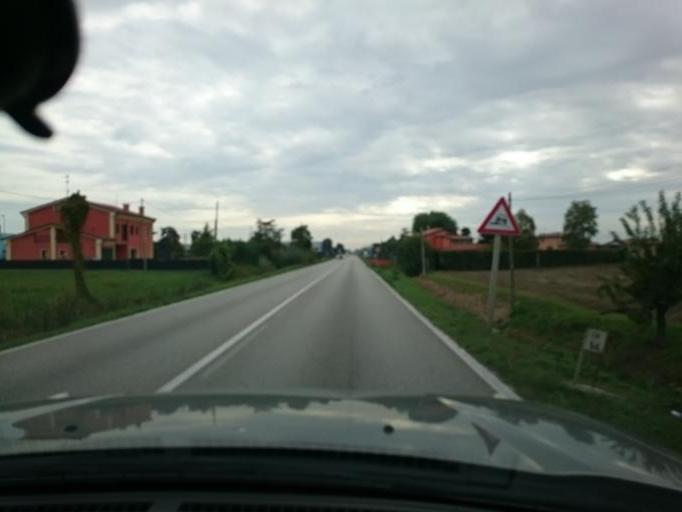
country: IT
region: Veneto
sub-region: Provincia di Padova
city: Sant'Angelo di Piove di Sacco
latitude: 45.3138
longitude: 12.0103
